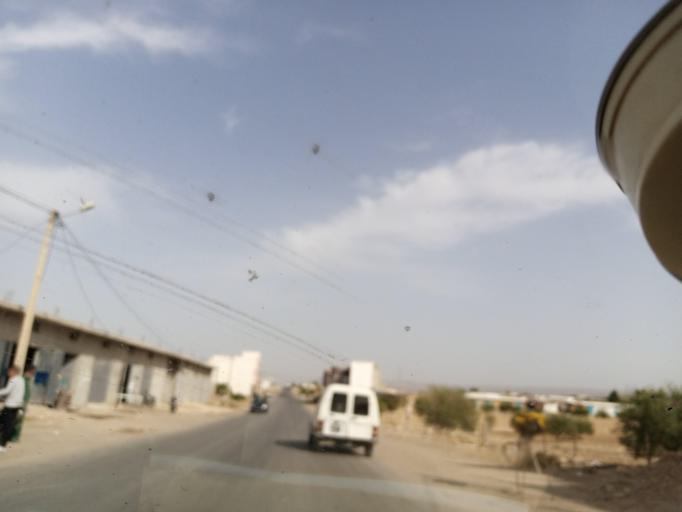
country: TN
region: Al Qasrayn
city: Kasserine
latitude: 35.2147
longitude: 8.9009
